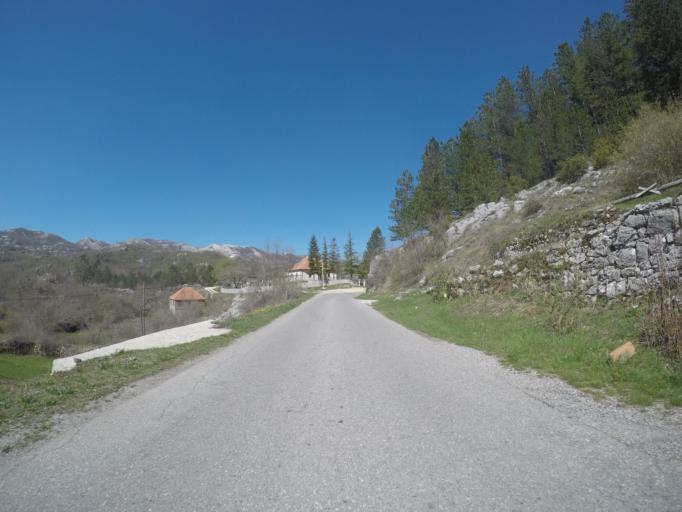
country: ME
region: Cetinje
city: Cetinje
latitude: 42.4639
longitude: 18.8618
